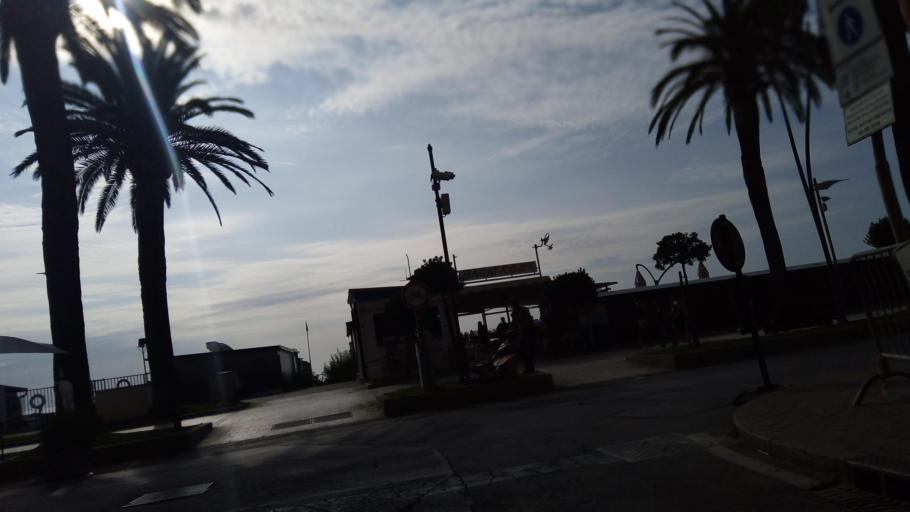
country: IT
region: Liguria
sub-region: Provincia di Savona
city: Ceriale
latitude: 44.0984
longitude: 8.2346
